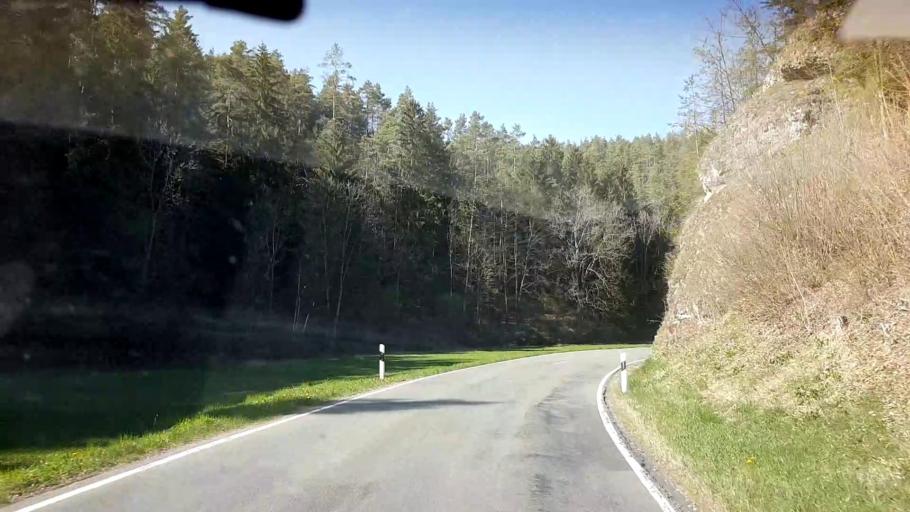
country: DE
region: Bavaria
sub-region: Upper Franconia
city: Pottenstein
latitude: 49.7817
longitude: 11.4184
